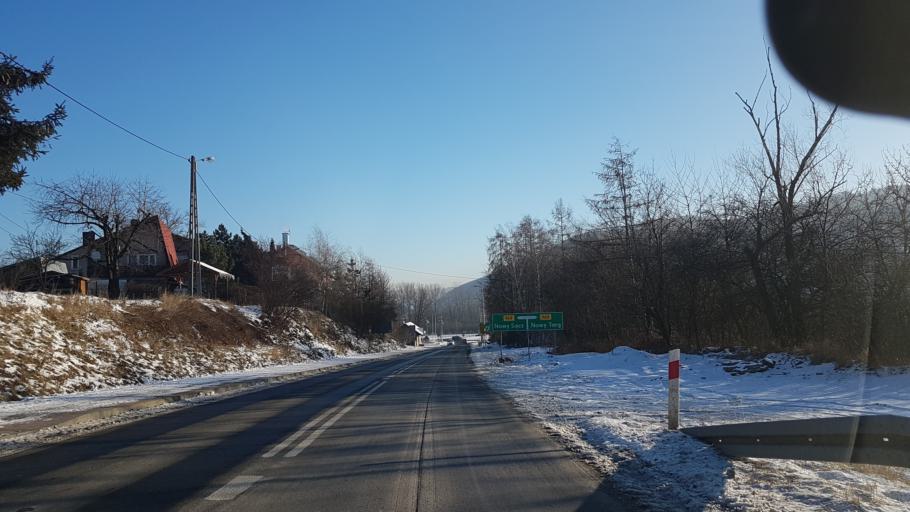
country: PL
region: Lesser Poland Voivodeship
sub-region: Powiat nowosadecki
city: Lacko
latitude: 49.5451
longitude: 20.4016
